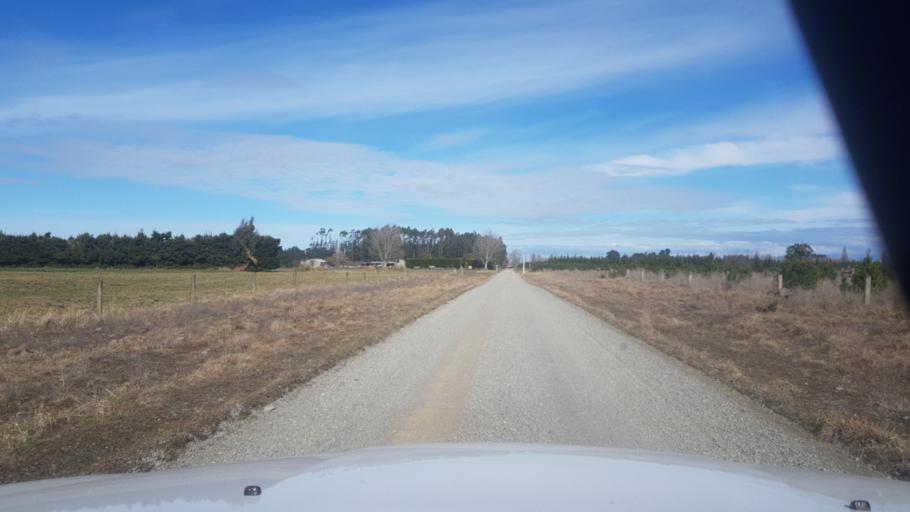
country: NZ
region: Canterbury
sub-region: Timaru District
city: Pleasant Point
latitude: -44.1351
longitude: 171.2786
